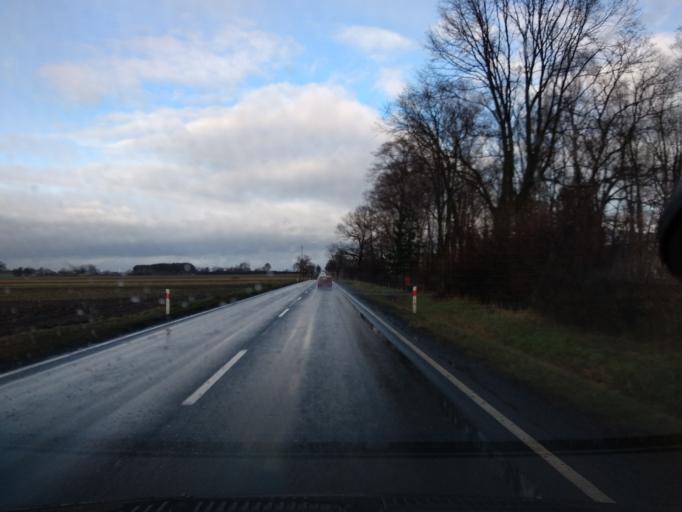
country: PL
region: Greater Poland Voivodeship
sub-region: Powiat koninski
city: Rychwal
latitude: 52.0453
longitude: 18.1623
